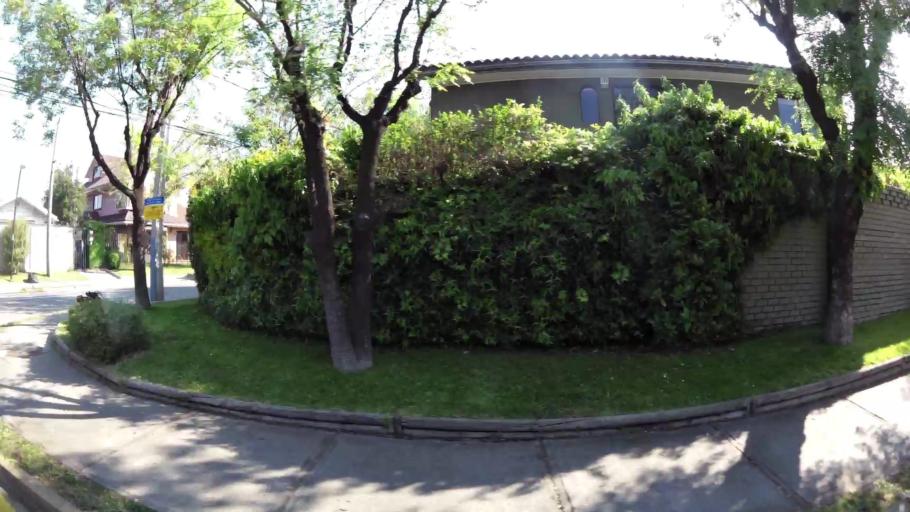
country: CL
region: Santiago Metropolitan
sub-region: Provincia de Santiago
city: Villa Presidente Frei, Nunoa, Santiago, Chile
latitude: -33.3807
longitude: -70.5560
